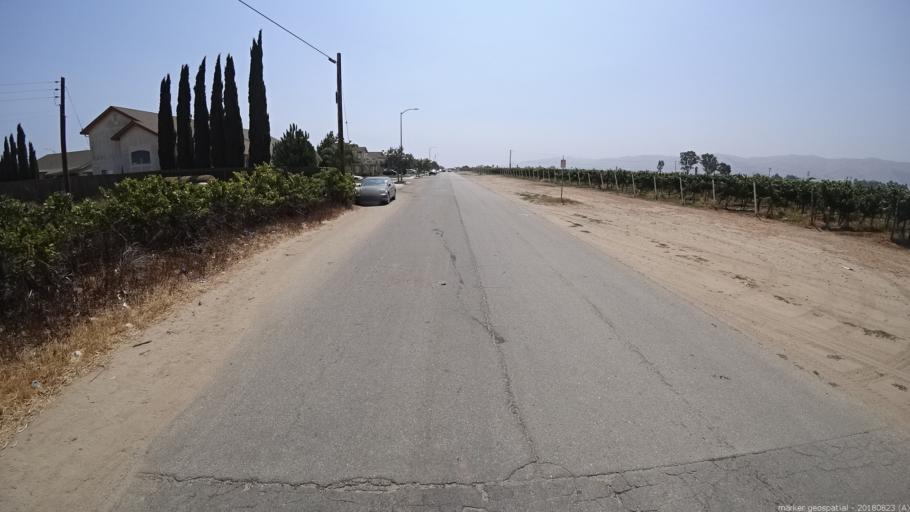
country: US
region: California
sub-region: Monterey County
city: Greenfield
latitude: 36.3243
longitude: -121.2572
